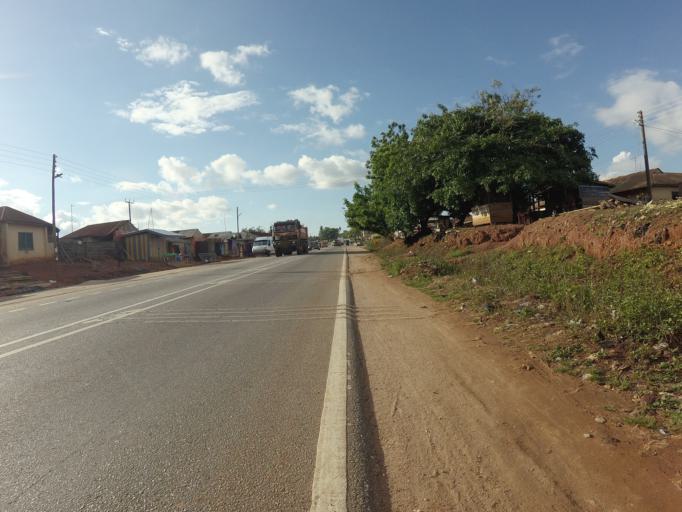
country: GH
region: Ashanti
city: Tafo
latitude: 6.9057
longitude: -1.6555
